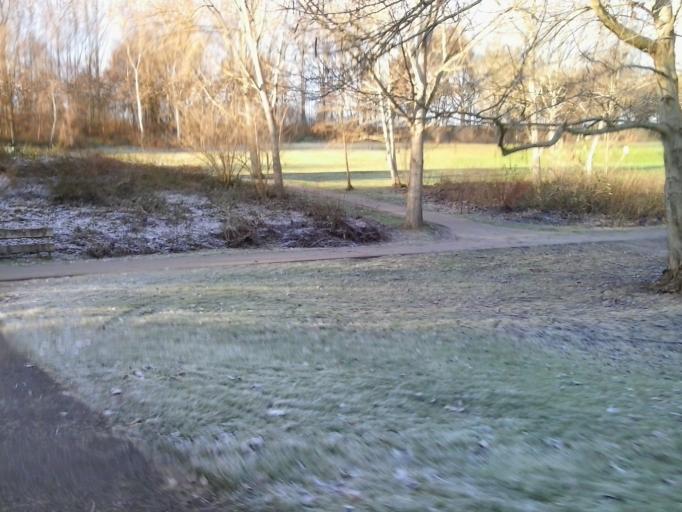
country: NL
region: South Holland
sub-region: Gemeente Lansingerland
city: Bergschenhoek
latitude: 51.9715
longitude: 4.5272
